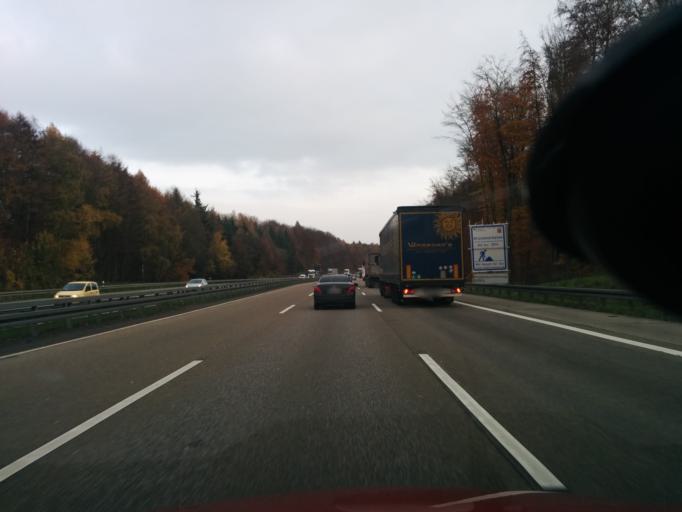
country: DE
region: Rheinland-Pfalz
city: Hambach
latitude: 50.4123
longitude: 7.9821
